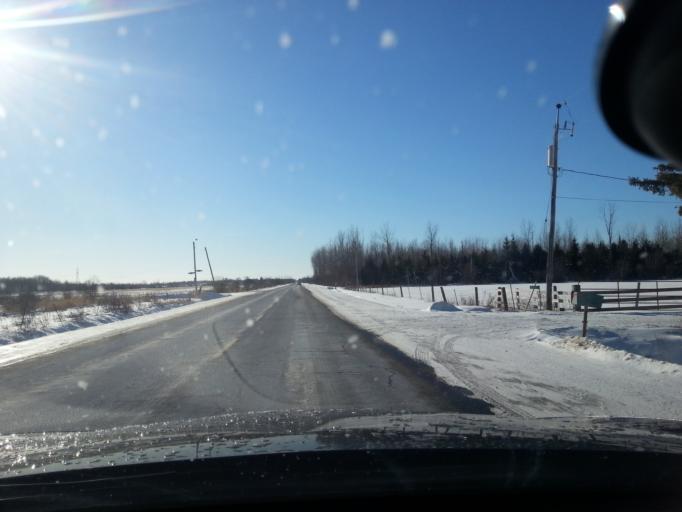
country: CA
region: Ontario
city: Ottawa
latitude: 45.3315
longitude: -75.4451
